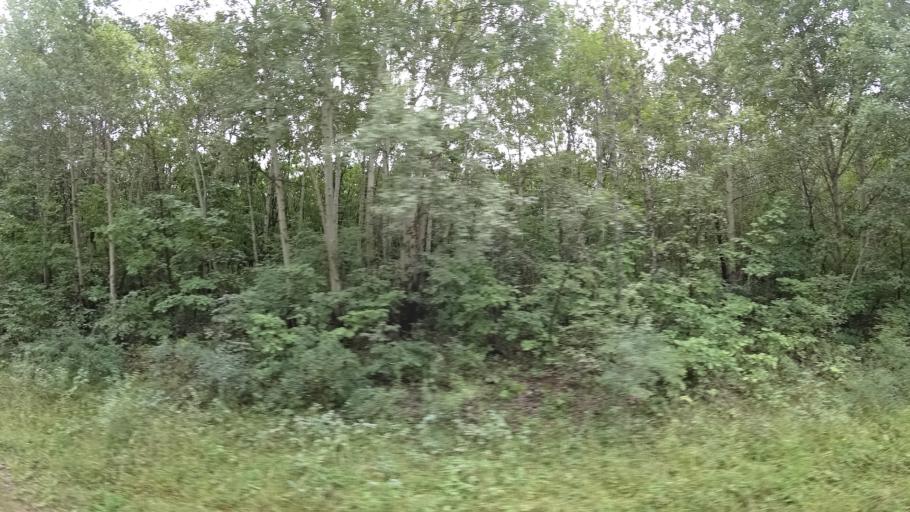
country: RU
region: Primorskiy
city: Lyalichi
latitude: 44.0849
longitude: 132.4424
